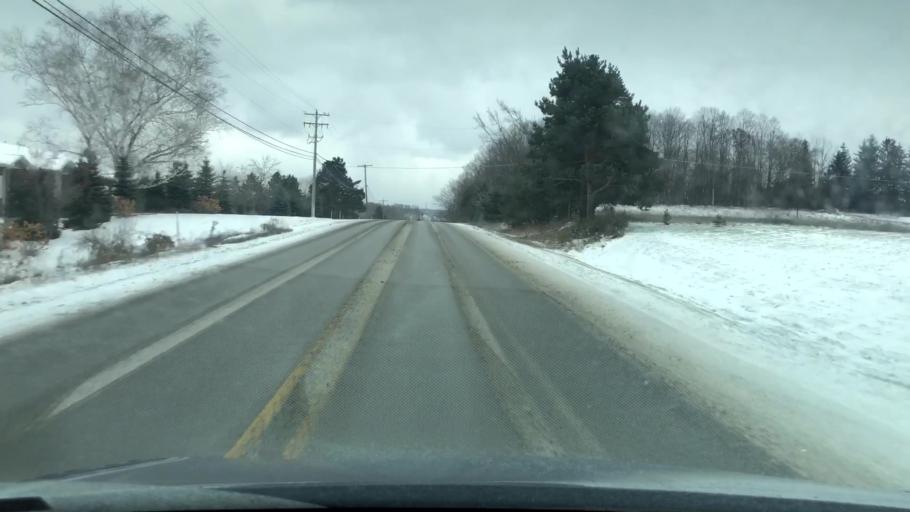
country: US
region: Michigan
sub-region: Grand Traverse County
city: Traverse City
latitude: 44.7154
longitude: -85.6330
